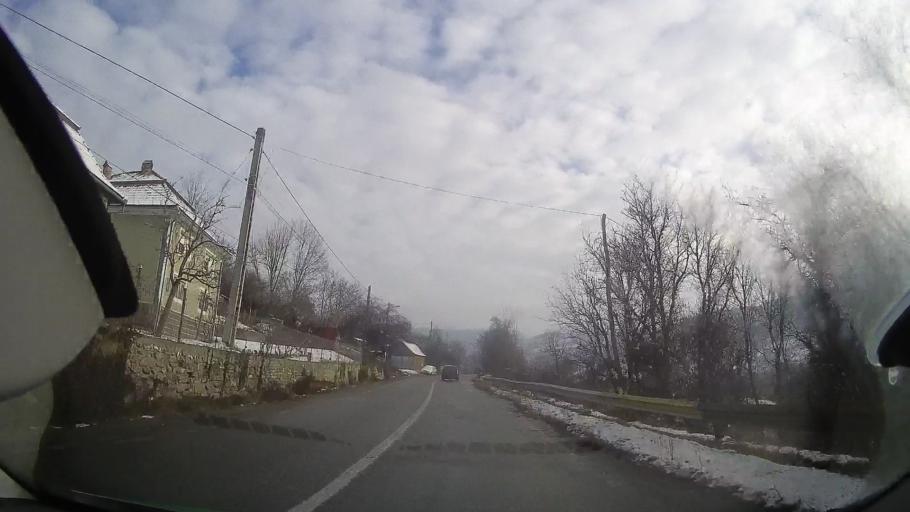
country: RO
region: Alba
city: Salciua de Sus
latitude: 46.3927
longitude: 23.3908
